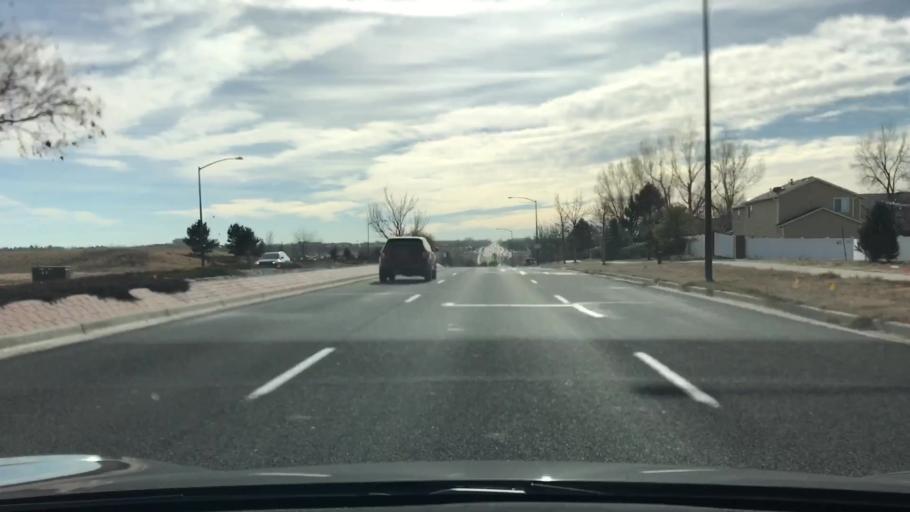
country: US
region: Colorado
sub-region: Adams County
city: Northglenn
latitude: 39.9395
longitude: -104.9968
